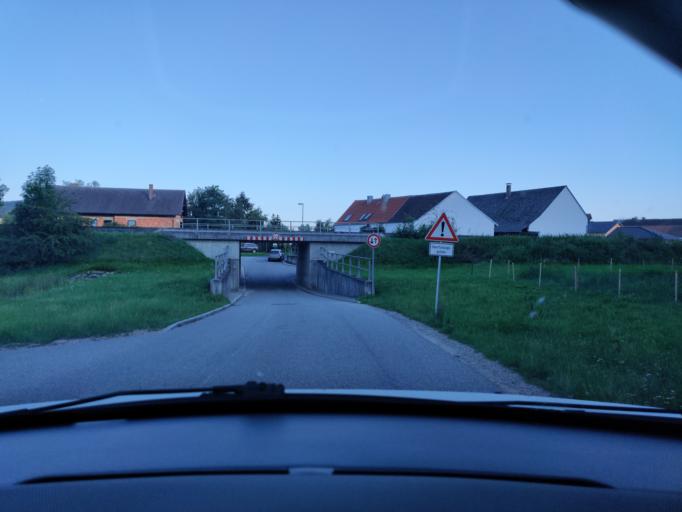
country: DE
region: Bavaria
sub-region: Upper Palatinate
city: Stulln
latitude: 49.4141
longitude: 12.1593
